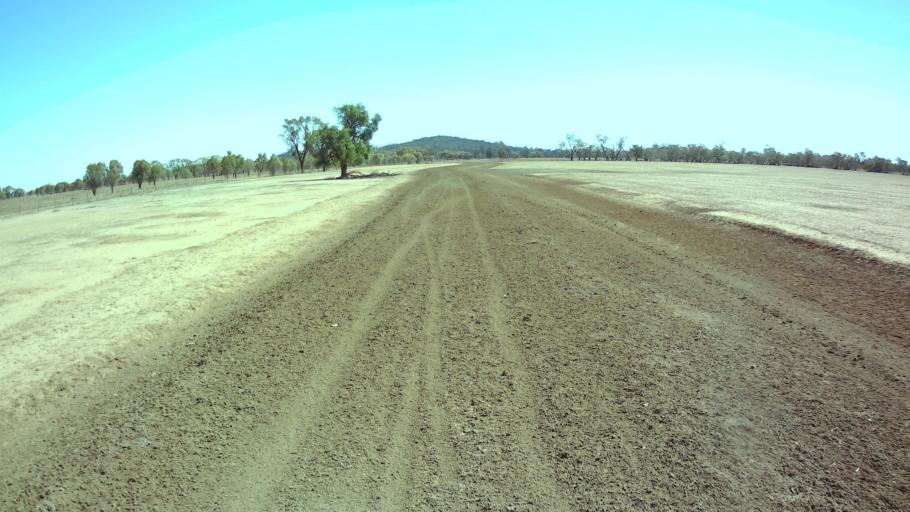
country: AU
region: New South Wales
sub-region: Bland
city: West Wyalong
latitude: -33.7545
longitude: 147.6592
